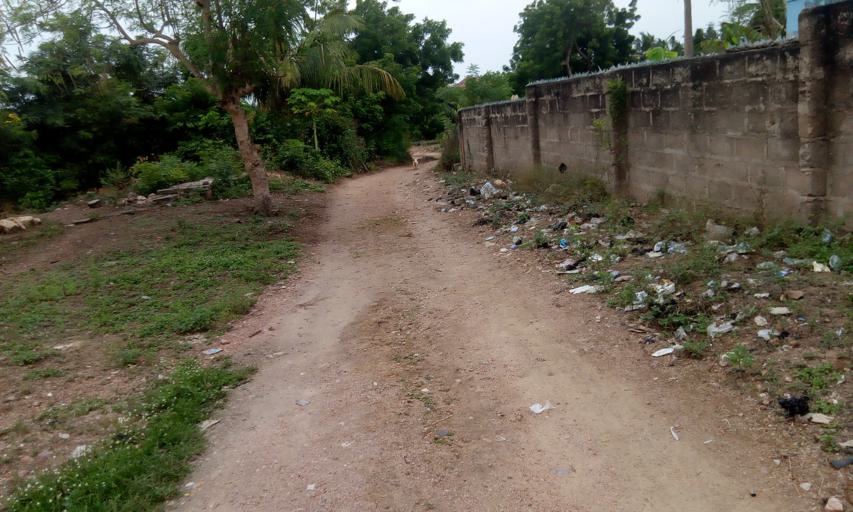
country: GH
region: Central
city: Winneba
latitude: 5.3543
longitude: -0.6256
